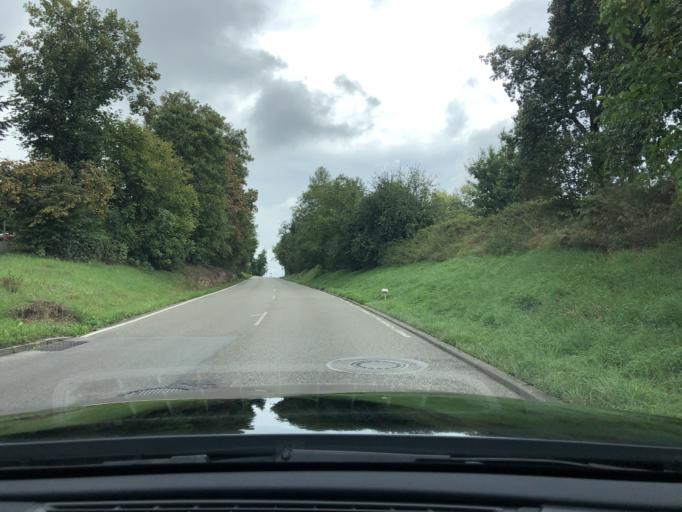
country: DE
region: Baden-Wuerttemberg
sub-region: Regierungsbezirk Stuttgart
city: Marbach am Neckar
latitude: 48.9368
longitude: 9.2683
